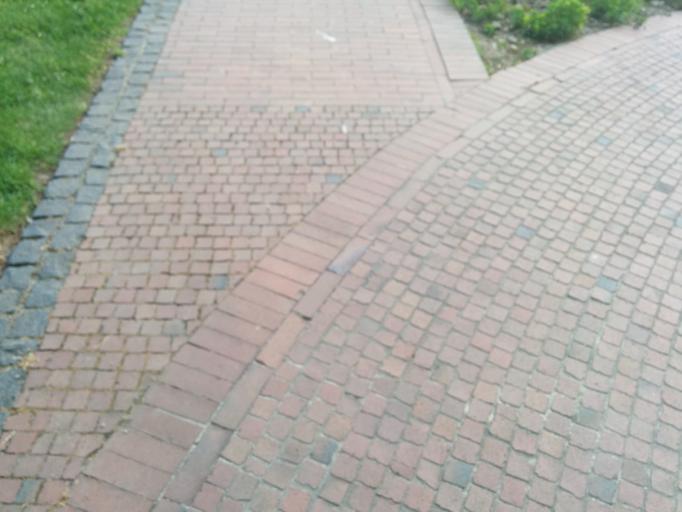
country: DE
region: Saxony-Anhalt
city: Bad Schmiedeberg
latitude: 51.6806
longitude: 12.7265
